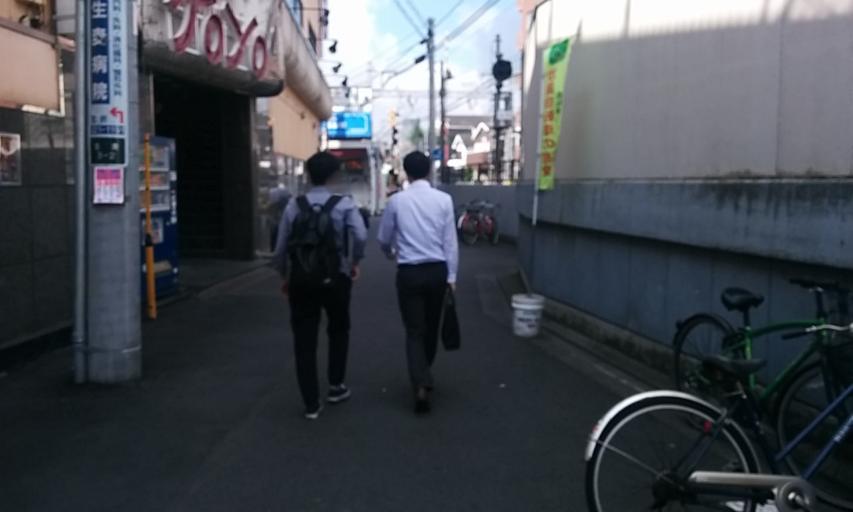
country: JP
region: Kanagawa
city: Yokohama
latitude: 35.4951
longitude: 139.6668
